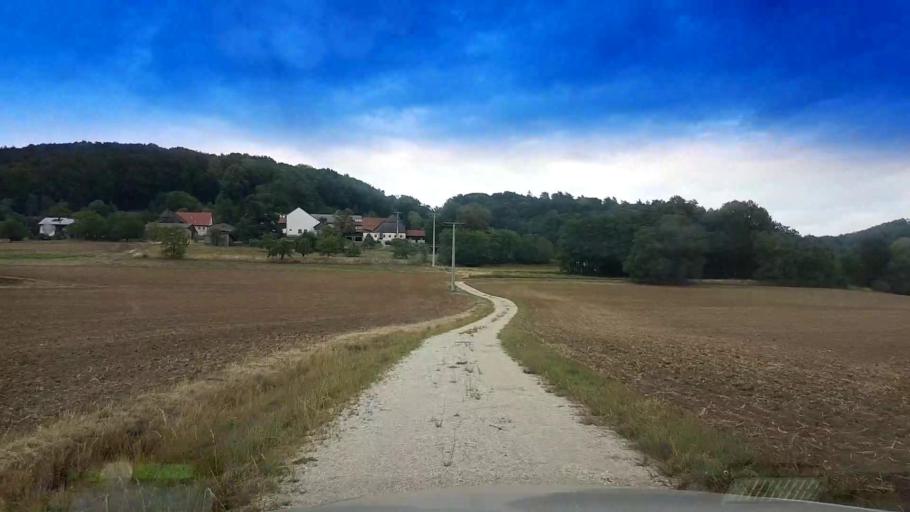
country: DE
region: Bavaria
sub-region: Upper Franconia
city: Schesslitz
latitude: 49.9473
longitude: 11.0461
